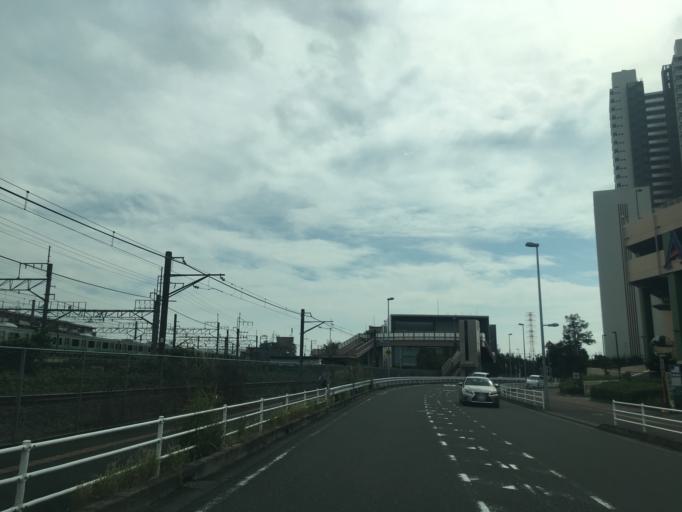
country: JP
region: Tokyo
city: Hachioji
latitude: 35.5915
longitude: 139.3511
